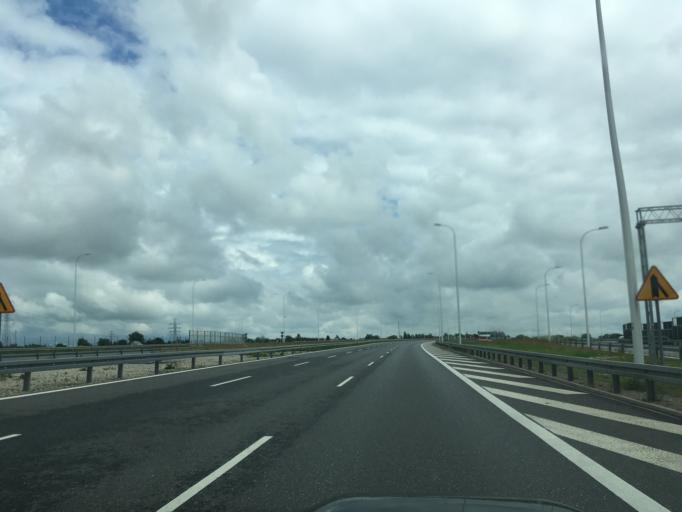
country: PL
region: Lublin Voivodeship
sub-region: Powiat lubelski
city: Lublin
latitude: 51.3027
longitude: 22.5803
